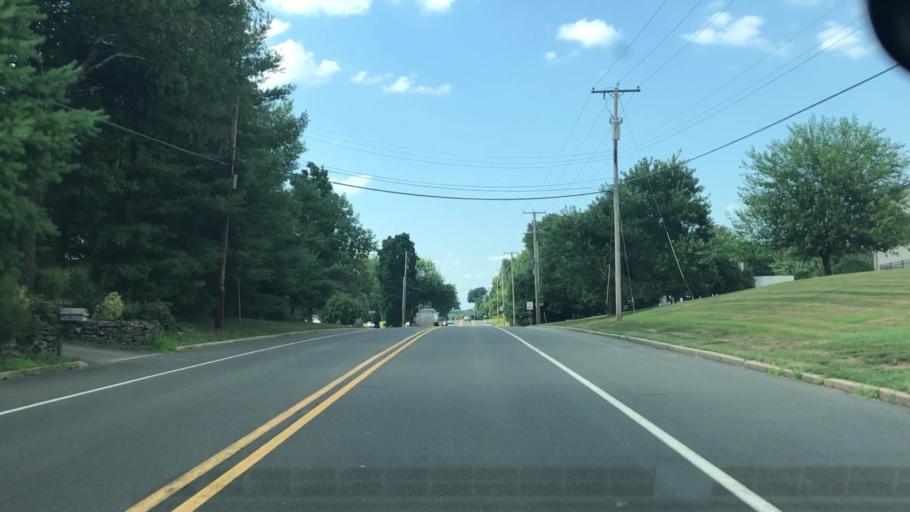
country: US
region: New Jersey
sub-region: Hunterdon County
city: Flemington
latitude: 40.5058
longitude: -74.8084
